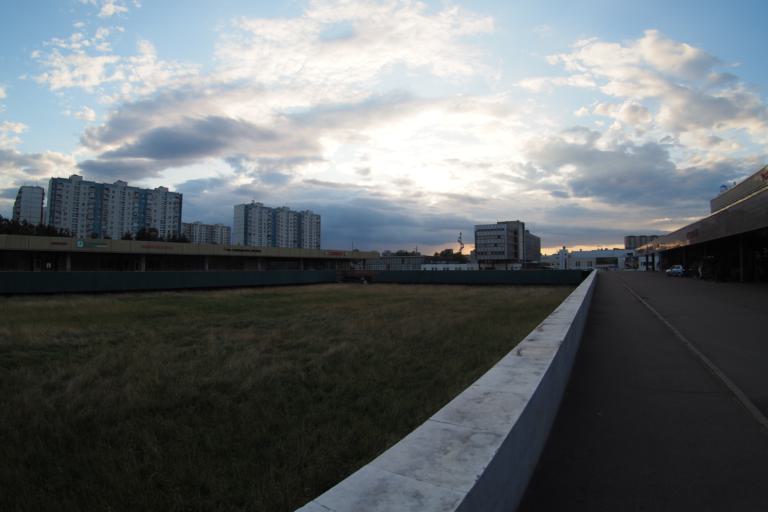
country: RU
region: Moscow
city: Nikulino
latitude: 55.6758
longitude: 37.4703
